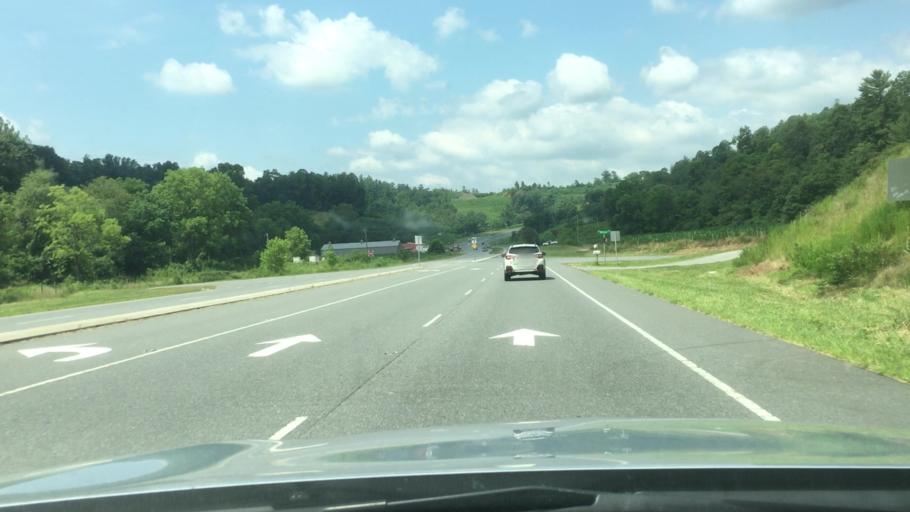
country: US
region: North Carolina
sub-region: Madison County
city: Mars Hill
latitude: 35.8427
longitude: -82.5034
